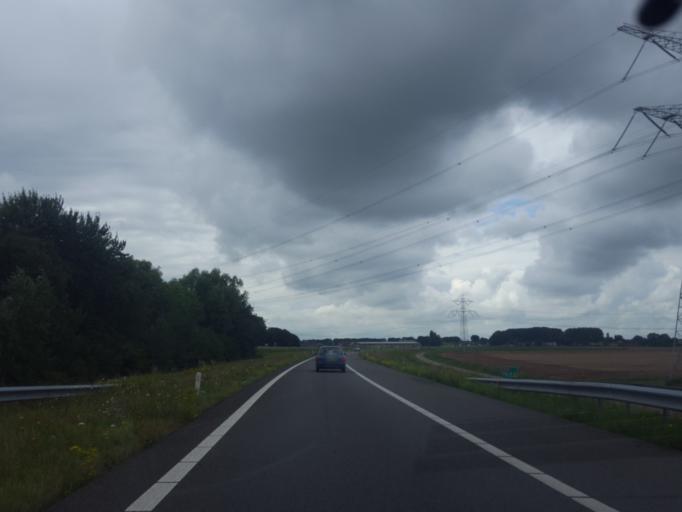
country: NL
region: North Brabant
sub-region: Gemeente Moerdijk
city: Klundert
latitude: 51.6364
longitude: 4.5418
